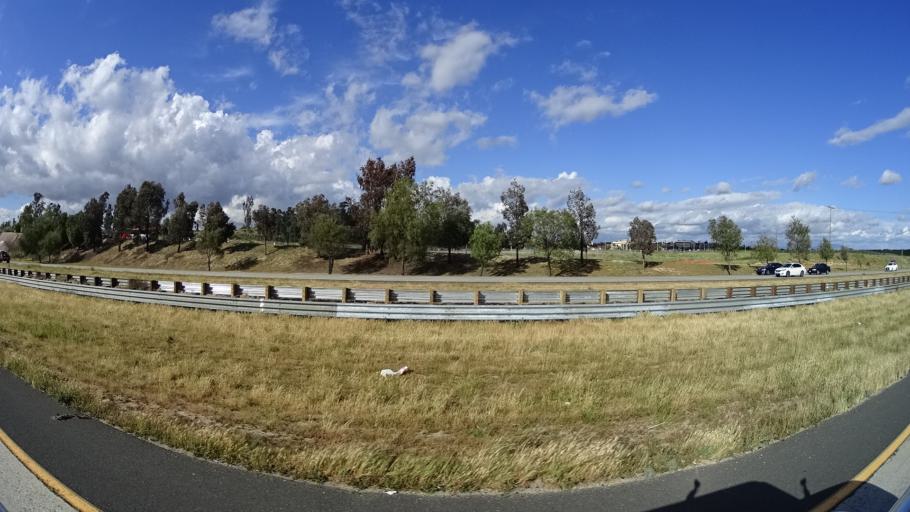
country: US
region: California
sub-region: Riverside County
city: Murrieta
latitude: 33.5537
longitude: -117.1905
